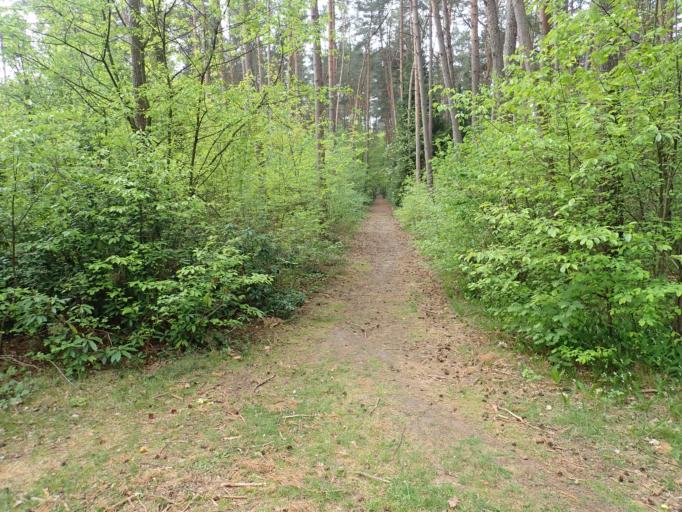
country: BE
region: Flanders
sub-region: Provincie Antwerpen
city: Herentals
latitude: 51.2019
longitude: 4.8477
